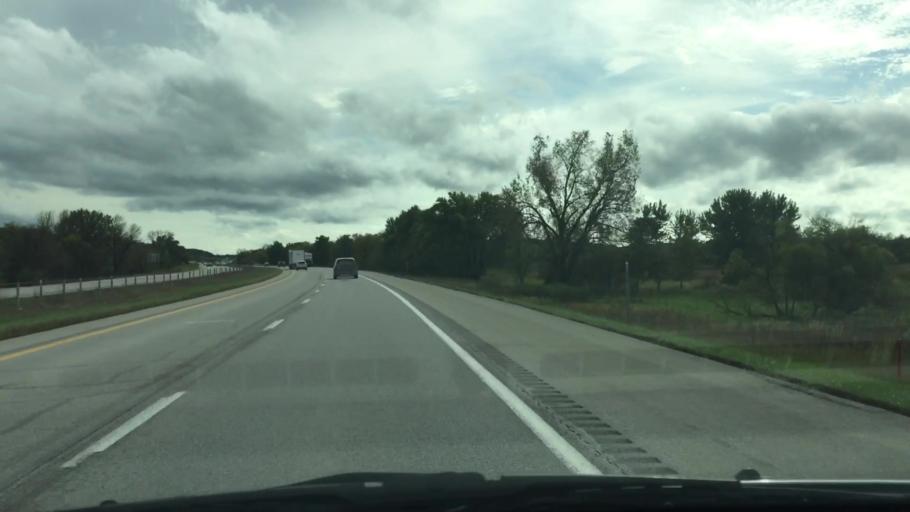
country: US
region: Iowa
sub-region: Clarke County
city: Osceola
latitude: 41.0849
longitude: -93.7812
